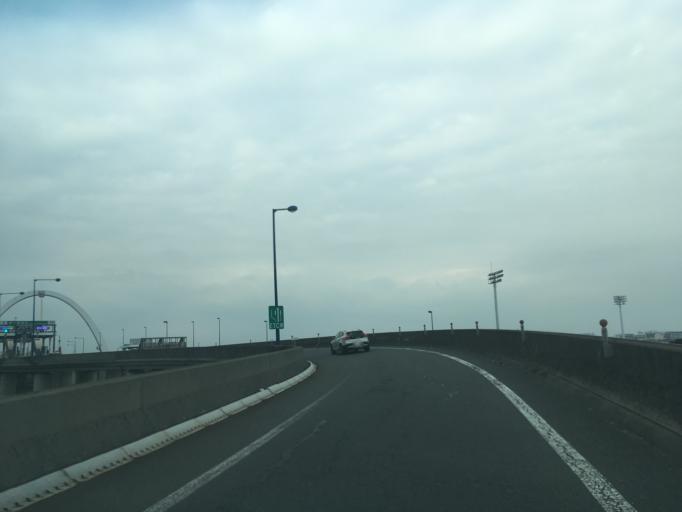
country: JP
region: Kanagawa
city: Chigasaki
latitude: 35.3221
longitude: 139.3754
